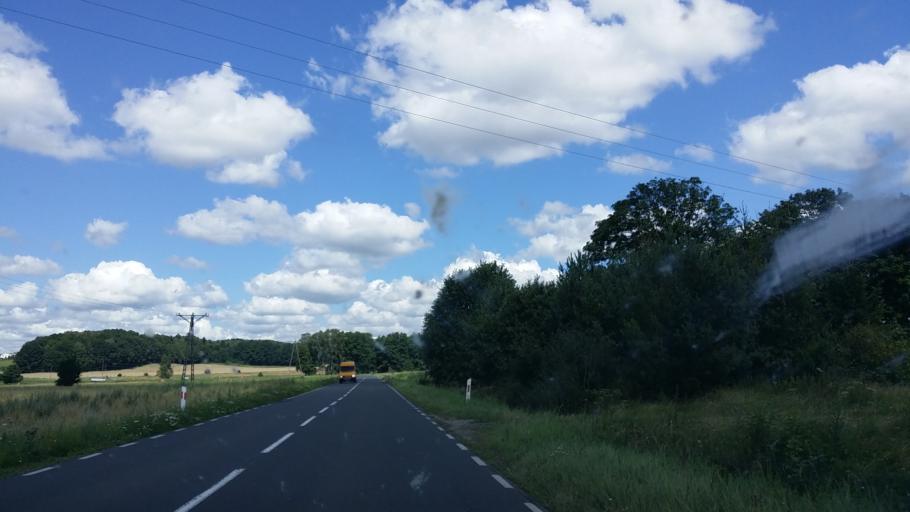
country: PL
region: West Pomeranian Voivodeship
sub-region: Powiat swidwinski
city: Swidwin
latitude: 53.7997
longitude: 15.7791
